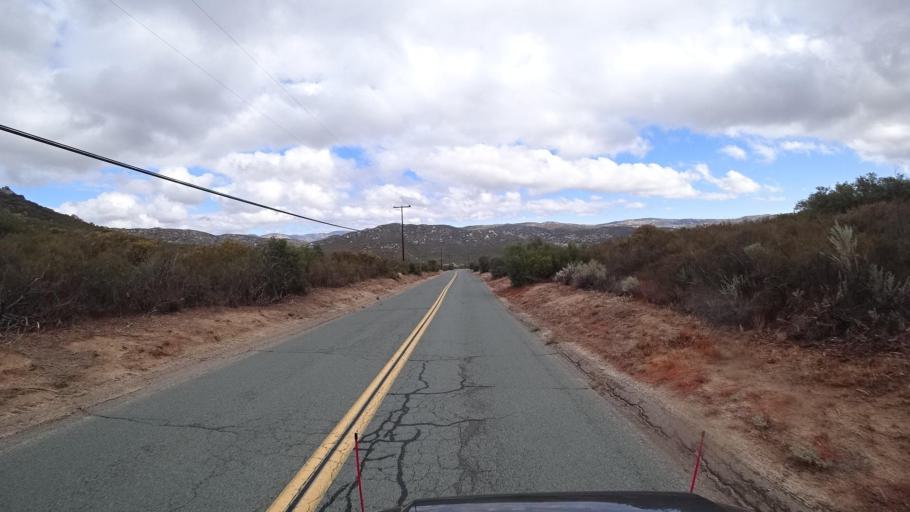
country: US
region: California
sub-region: San Diego County
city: Campo
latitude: 32.6749
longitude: -116.4299
